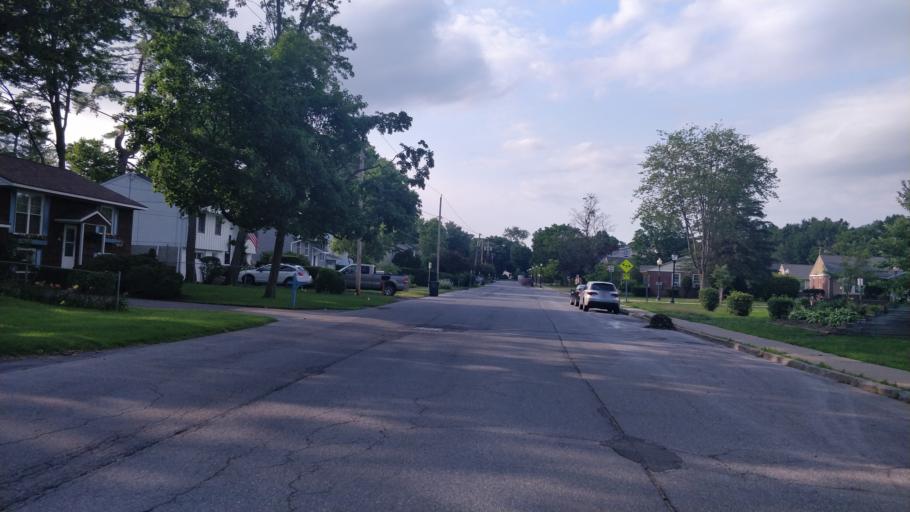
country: US
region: New York
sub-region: Saratoga County
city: Saratoga Springs
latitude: 43.0705
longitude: -73.7827
